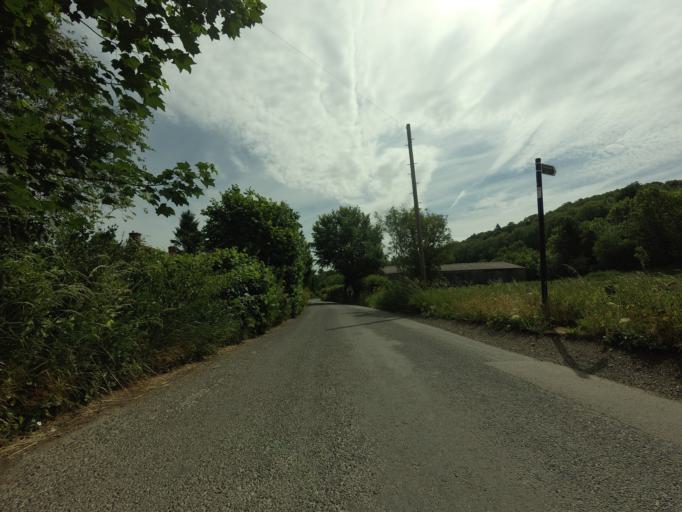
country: GB
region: England
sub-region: Kent
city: Shoreham
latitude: 51.3393
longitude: 0.1661
